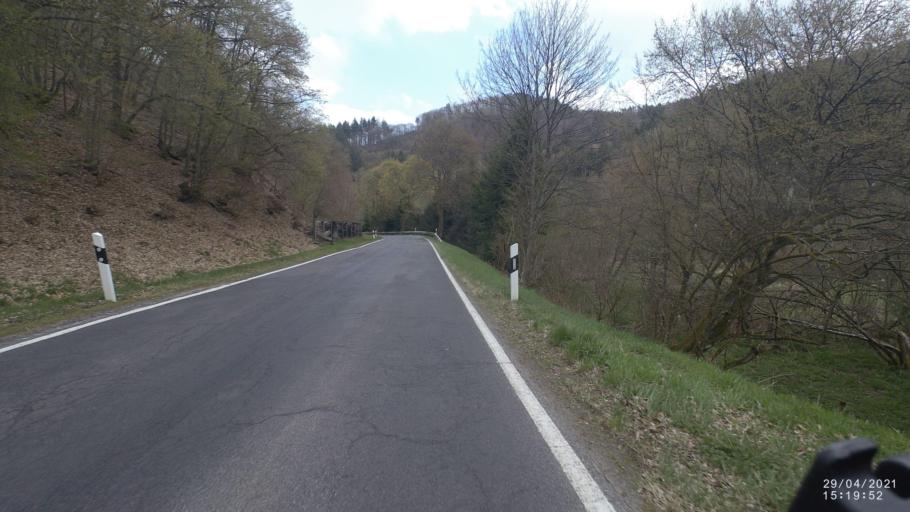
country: DE
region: Rheinland-Pfalz
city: Langscheid
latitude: 50.3791
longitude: 7.1278
